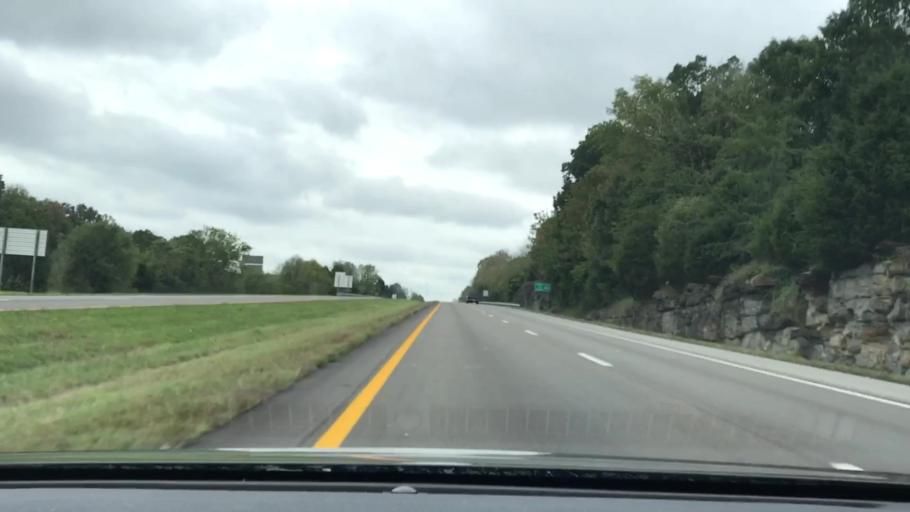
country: US
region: Kentucky
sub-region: Adair County
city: Columbia
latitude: 37.0801
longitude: -85.3210
